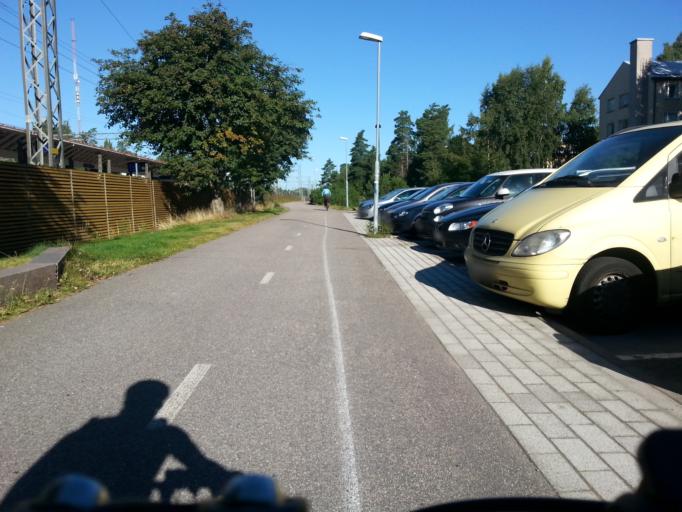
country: FI
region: Uusimaa
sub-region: Helsinki
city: Helsinki
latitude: 60.2185
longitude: 24.8941
